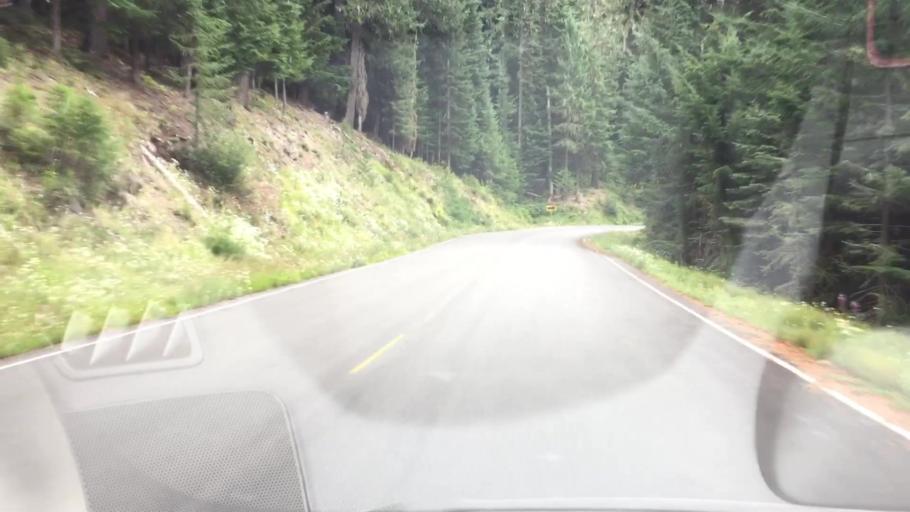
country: US
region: Washington
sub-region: Klickitat County
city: White Salmon
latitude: 46.2124
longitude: -121.6319
